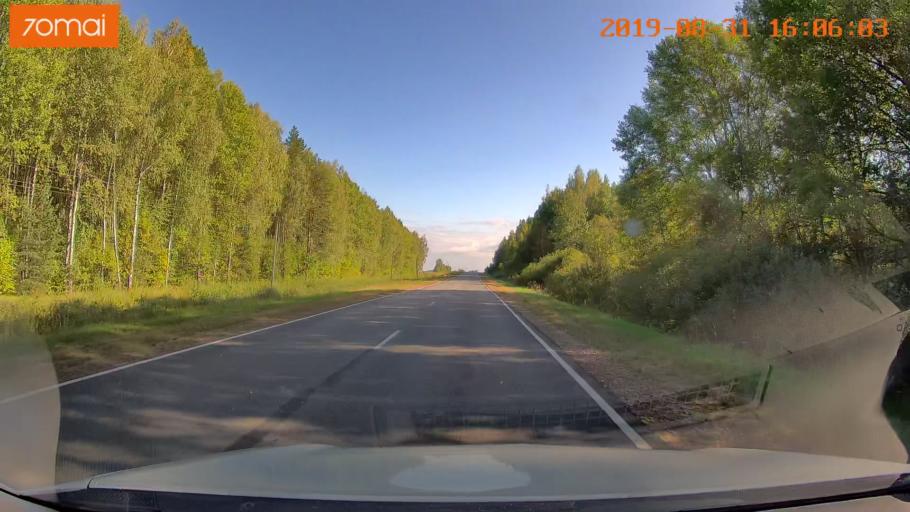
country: RU
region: Kaluga
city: Yukhnov
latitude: 54.6301
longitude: 35.3417
